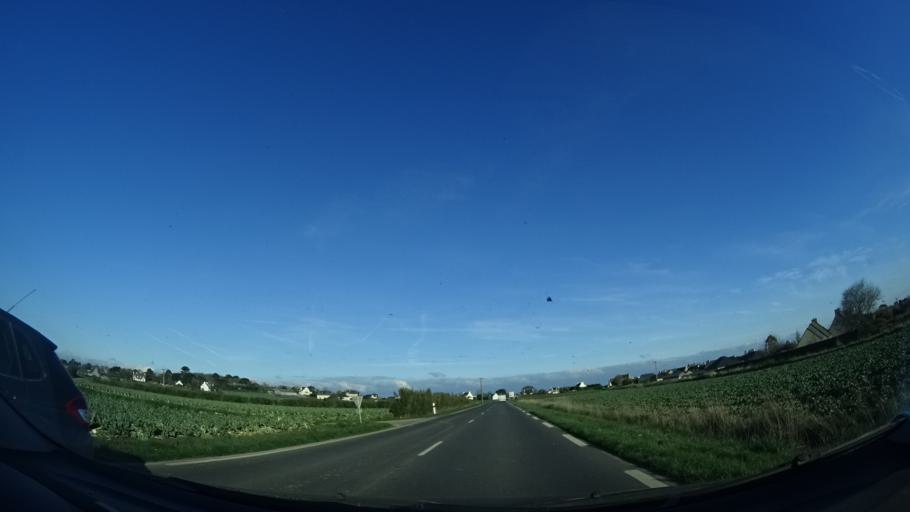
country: FR
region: Brittany
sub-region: Departement du Finistere
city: Saint-Pol-de-Leon
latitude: 48.7001
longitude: -3.9918
